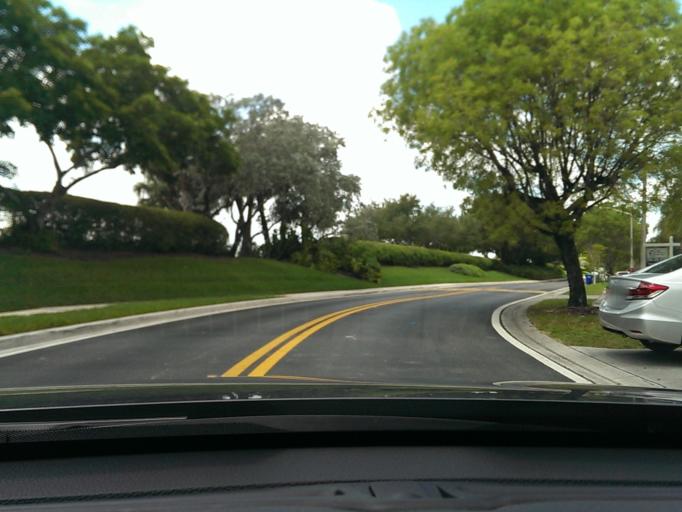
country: US
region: Florida
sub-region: Broward County
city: Sunshine Ranches
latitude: 26.0085
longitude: -80.3448
